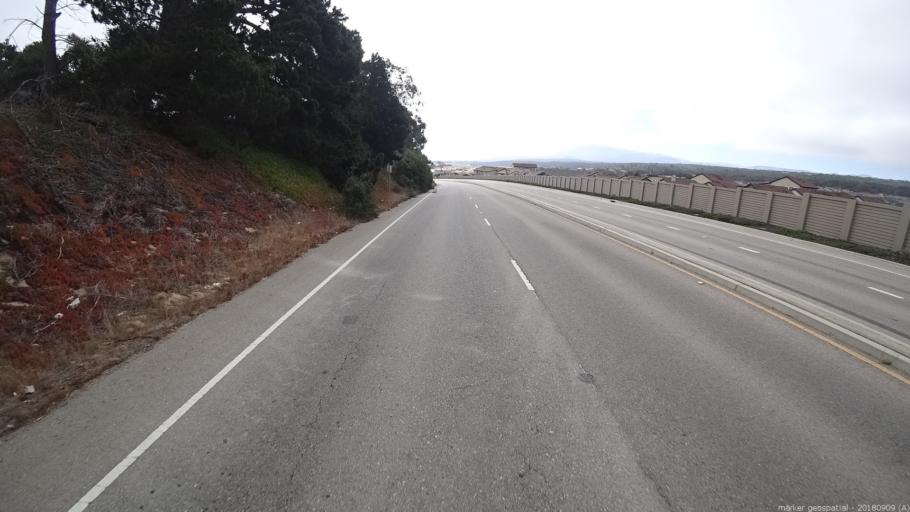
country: US
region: California
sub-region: Monterey County
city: Marina
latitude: 36.6569
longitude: -121.7358
